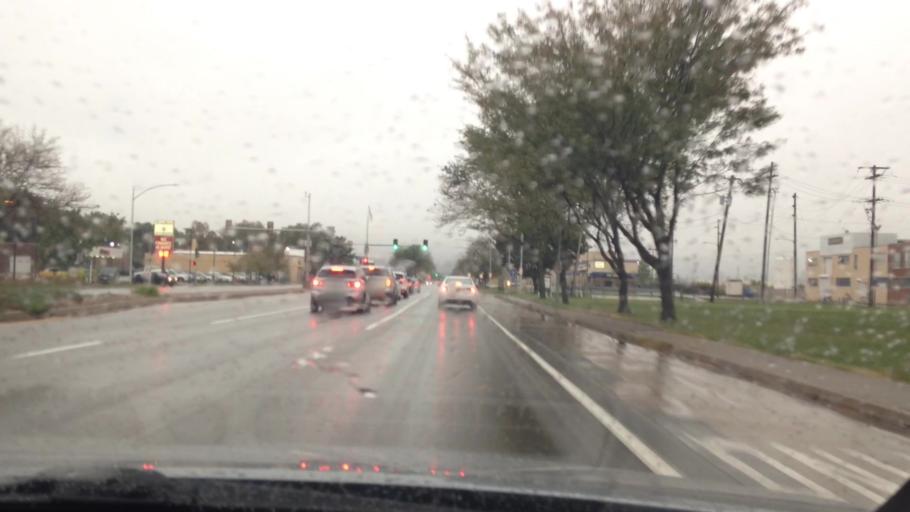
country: US
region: Missouri
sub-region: Clay County
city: North Kansas City
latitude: 39.1461
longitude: -94.5805
